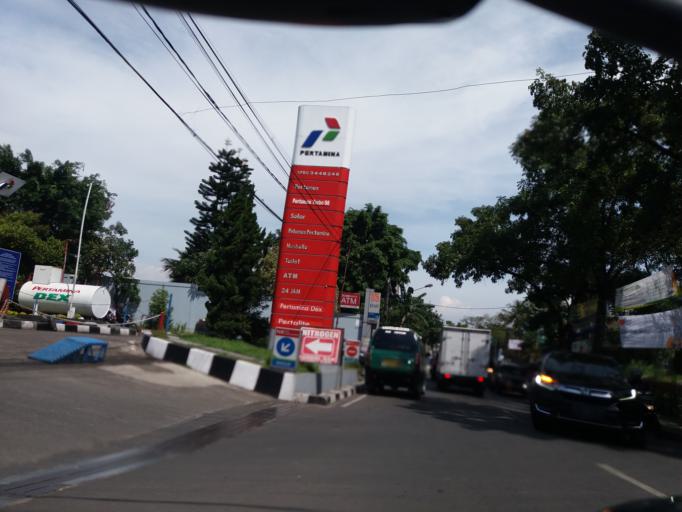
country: ID
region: West Java
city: Margahayukencana
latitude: -6.9264
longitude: 107.5747
